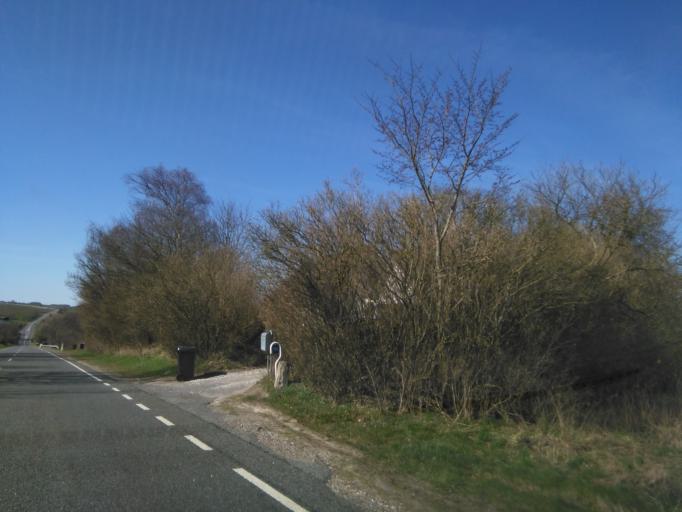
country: DK
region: Central Jutland
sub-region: Skanderborg Kommune
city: Skanderborg
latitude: 56.0261
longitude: 9.8435
